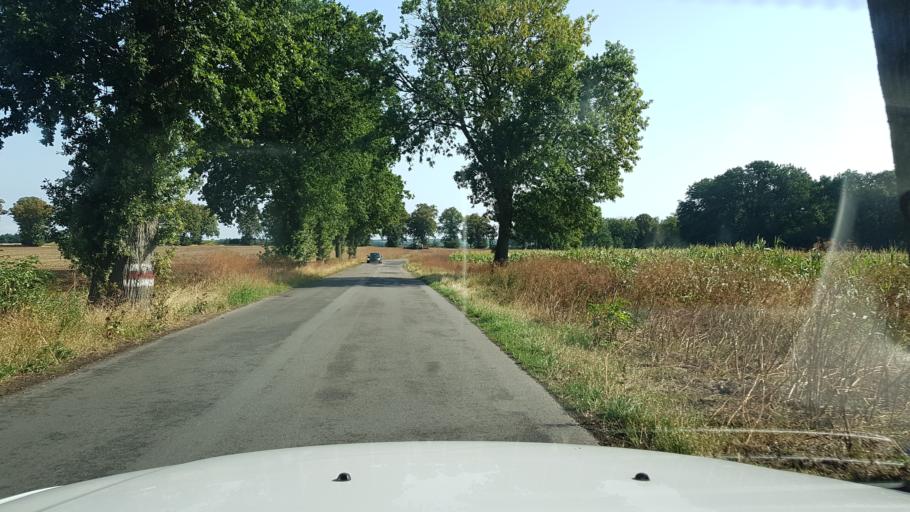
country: PL
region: West Pomeranian Voivodeship
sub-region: Powiat stargardzki
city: Stargard Szczecinski
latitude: 53.2702
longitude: 15.1232
